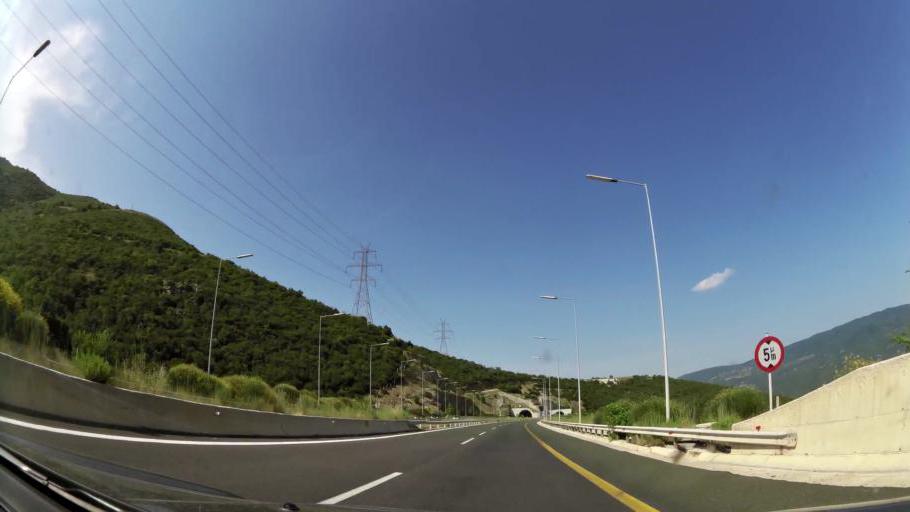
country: GR
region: Central Macedonia
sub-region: Nomos Imathias
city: Rizomata
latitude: 40.3981
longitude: 22.1630
